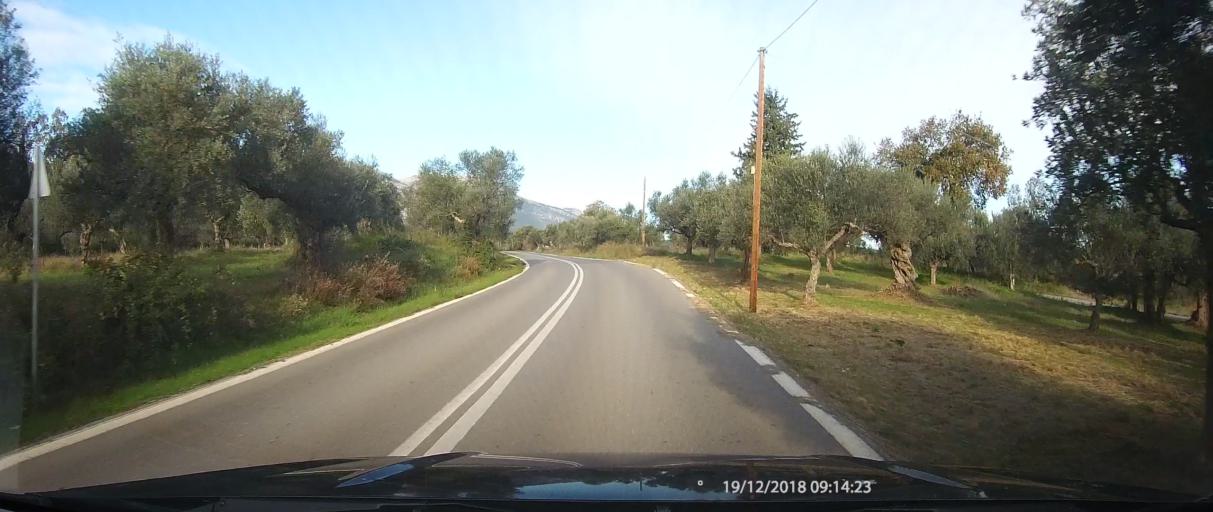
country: GR
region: Peloponnese
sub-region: Nomos Lakonias
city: Magoula
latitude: 37.0861
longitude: 22.3894
